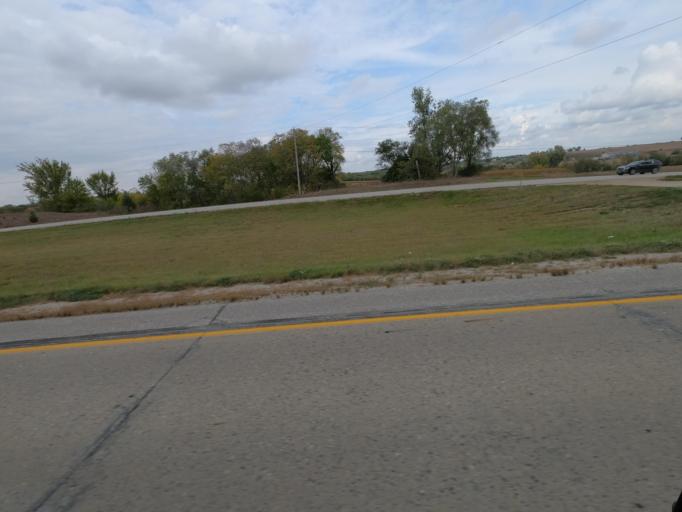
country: US
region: Iowa
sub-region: Polk County
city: Mitchellville
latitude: 41.6004
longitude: -93.3728
